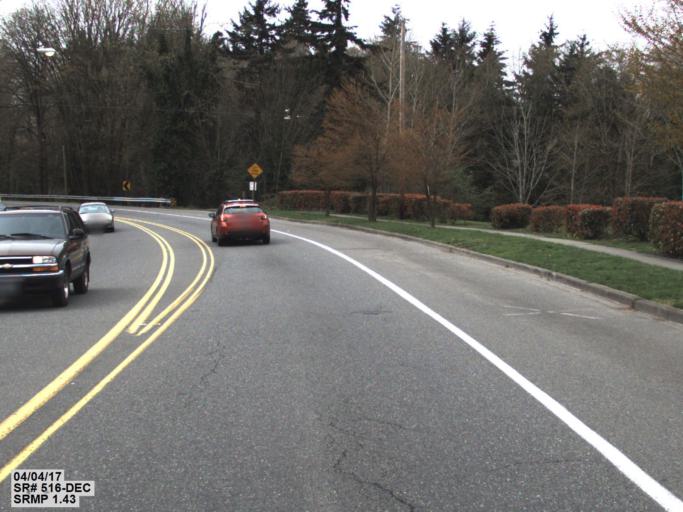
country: US
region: Washington
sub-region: King County
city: Des Moines
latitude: 47.3959
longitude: -122.3014
